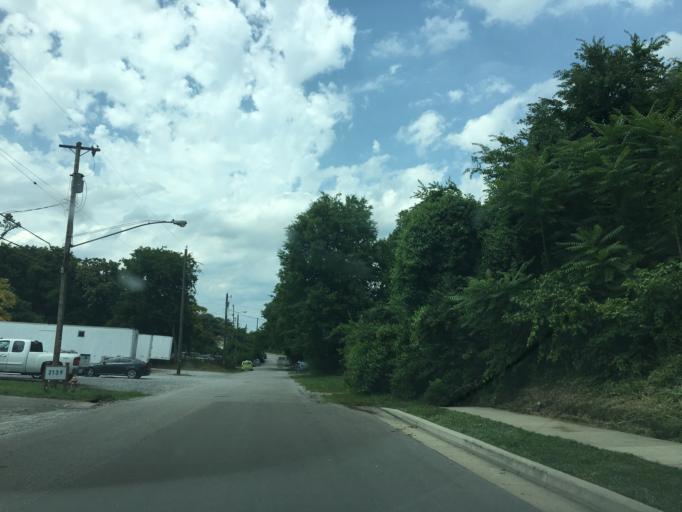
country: US
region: Tennessee
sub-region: Davidson County
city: Oak Hill
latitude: 36.1263
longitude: -86.7552
